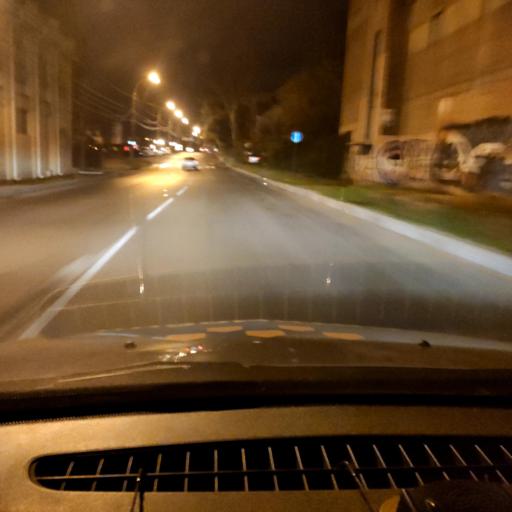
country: RU
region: Voronezj
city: Voronezh
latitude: 51.6600
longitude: 39.2161
